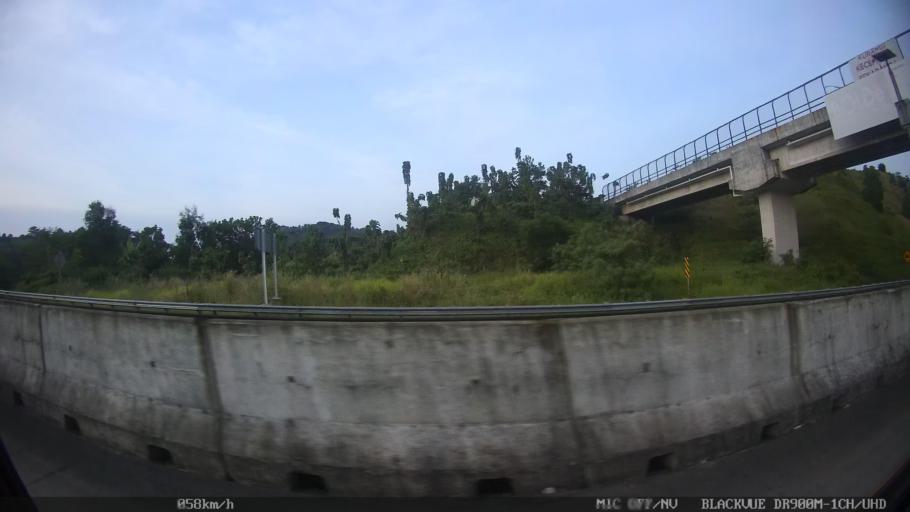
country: ID
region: Lampung
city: Penengahan
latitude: -5.8601
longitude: 105.7337
